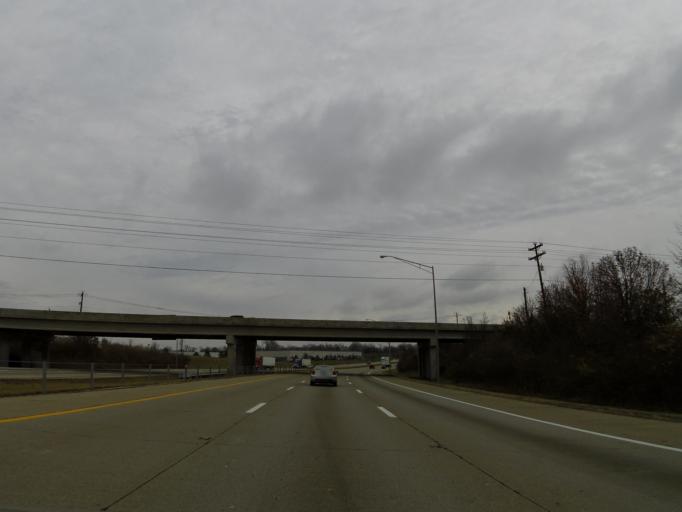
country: US
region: Kentucky
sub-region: Kenton County
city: Villa Hills
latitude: 39.0551
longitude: -84.6271
